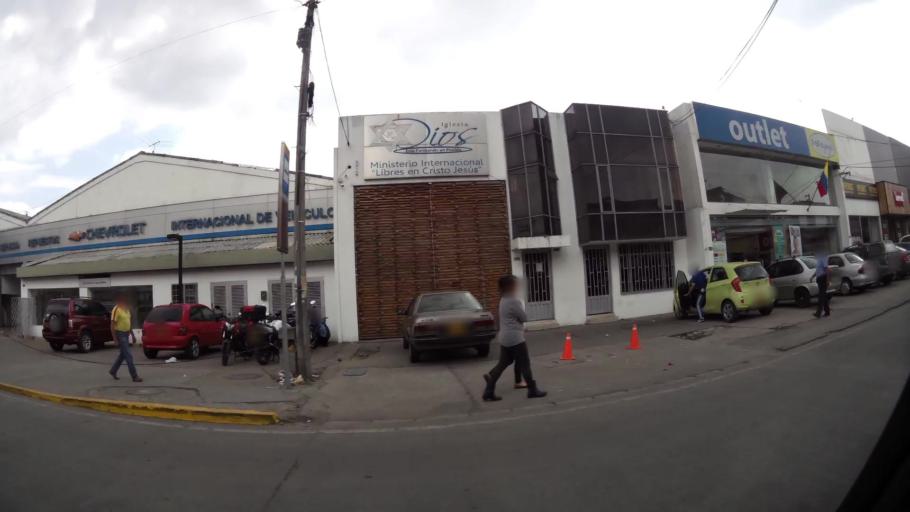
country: CO
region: Cundinamarca
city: La Calera
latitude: 4.7445
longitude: -74.0437
